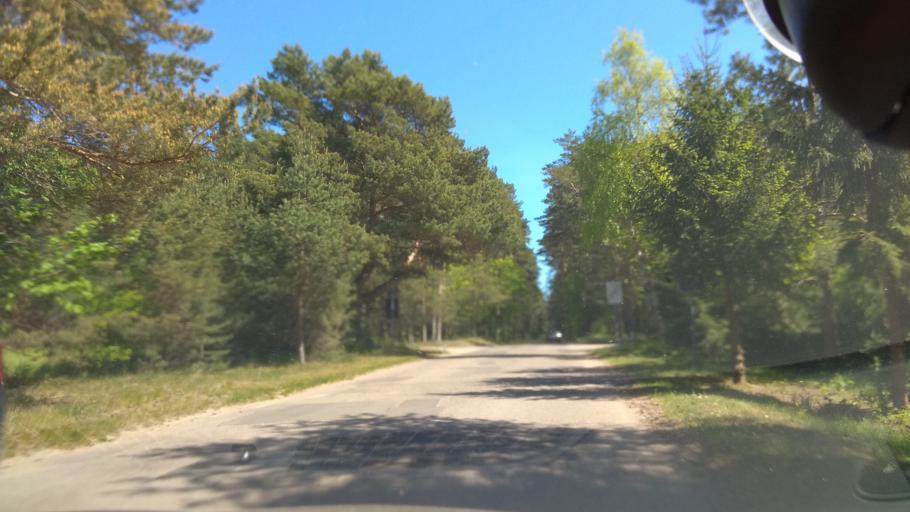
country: LT
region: Klaipedos apskritis
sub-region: Klaipeda
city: Palanga
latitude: 55.9478
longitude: 21.0793
